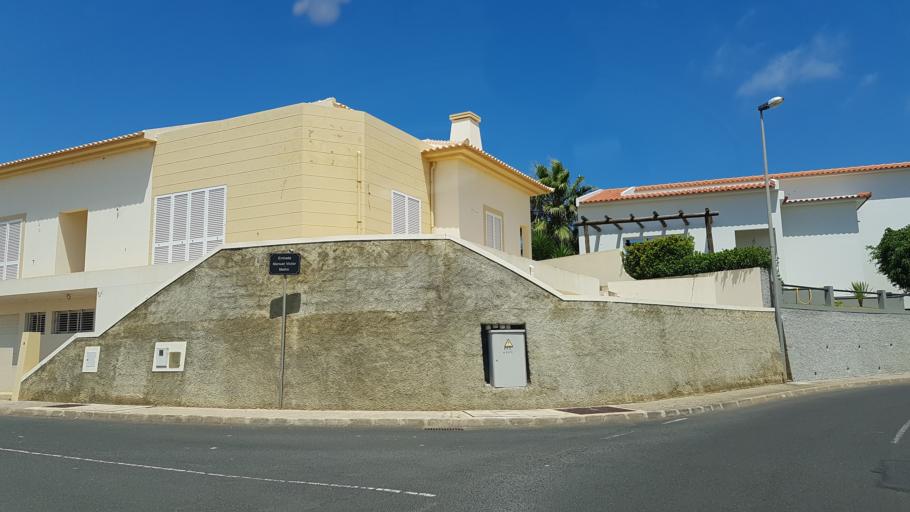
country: PT
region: Madeira
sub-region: Porto Santo
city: Vila de Porto Santo
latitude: 33.0551
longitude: -16.3564
